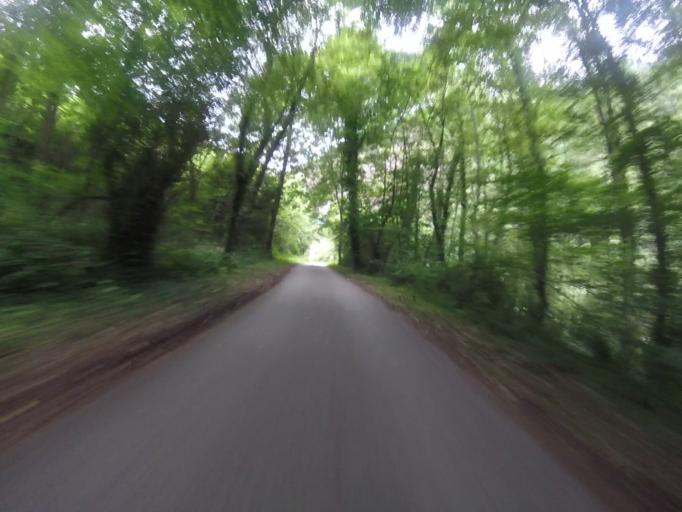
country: ES
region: Navarre
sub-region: Provincia de Navarra
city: Igantzi
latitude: 43.2176
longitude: -1.6715
